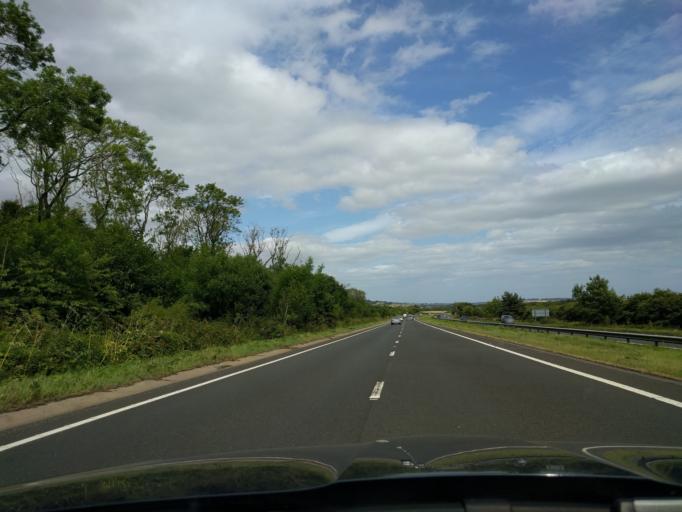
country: GB
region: England
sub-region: Northumberland
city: Alnwick
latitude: 55.3743
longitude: -1.7229
